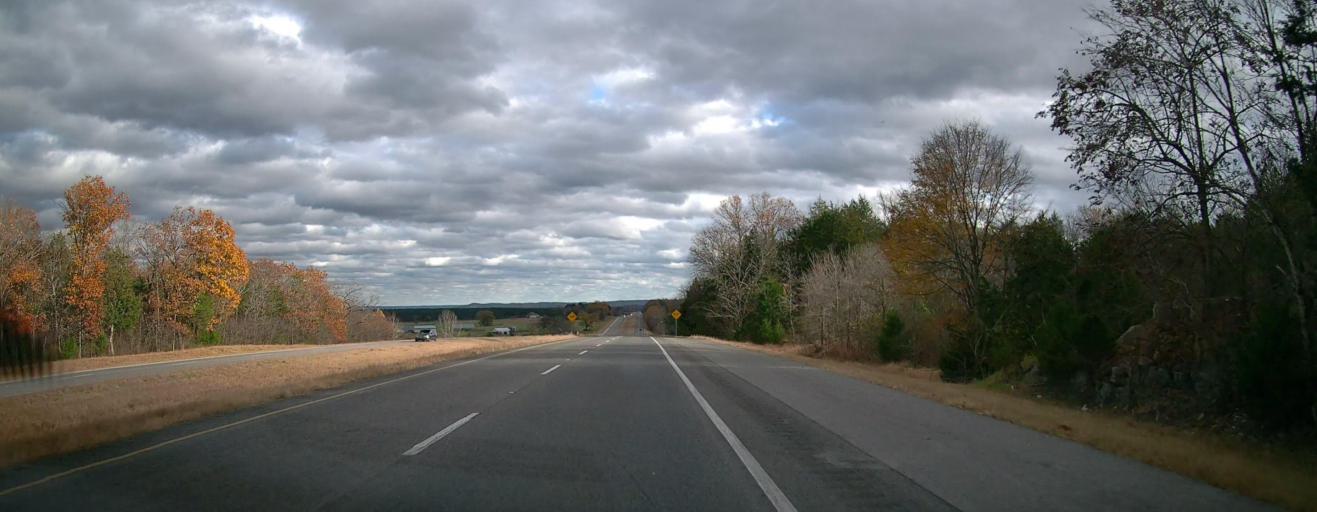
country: US
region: Alabama
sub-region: Morgan County
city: Danville
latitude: 34.3970
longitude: -87.1255
